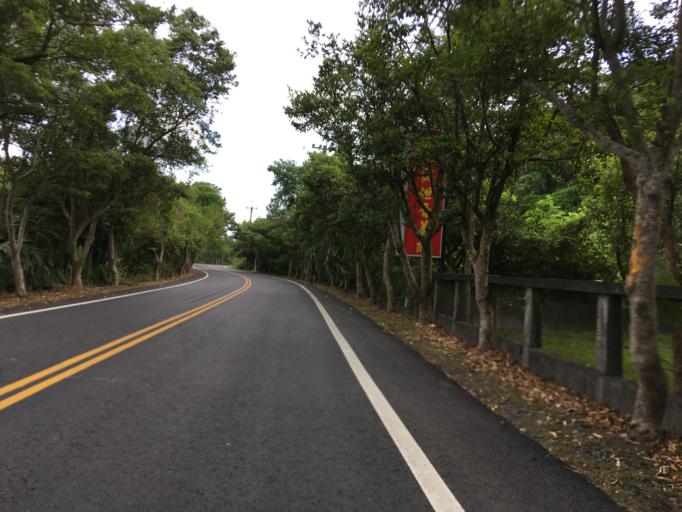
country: TW
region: Taiwan
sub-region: Yilan
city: Yilan
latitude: 24.6289
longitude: 121.7110
